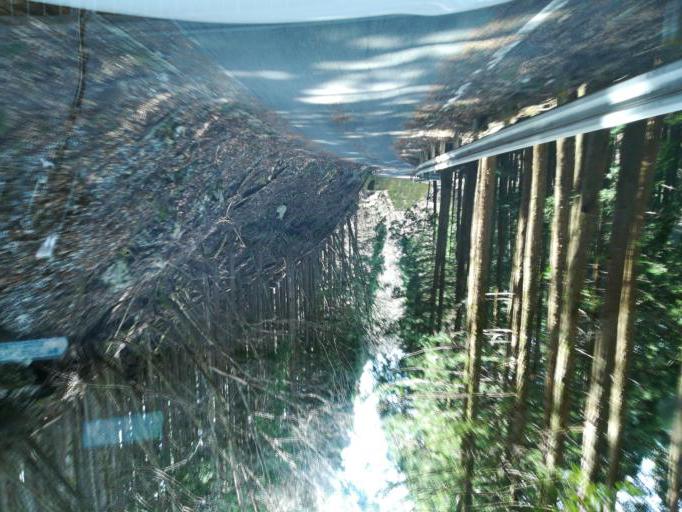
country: JP
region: Tokushima
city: Wakimachi
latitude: 33.8828
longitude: 134.0569
